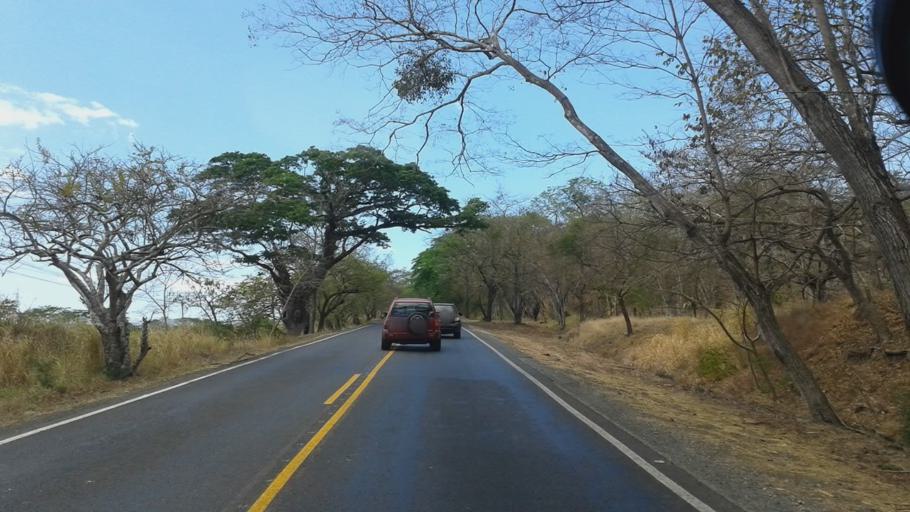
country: CR
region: Guanacaste
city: Juntas
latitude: 10.1398
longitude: -84.9070
